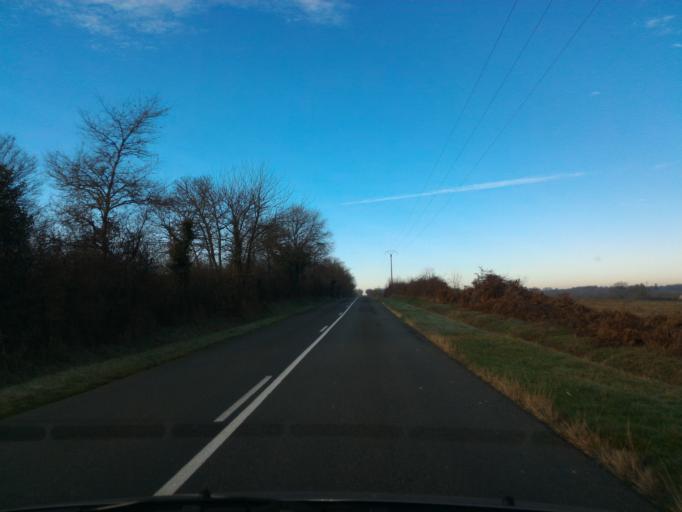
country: FR
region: Poitou-Charentes
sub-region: Departement de la Charente
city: Confolens
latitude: 46.0337
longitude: 0.6044
